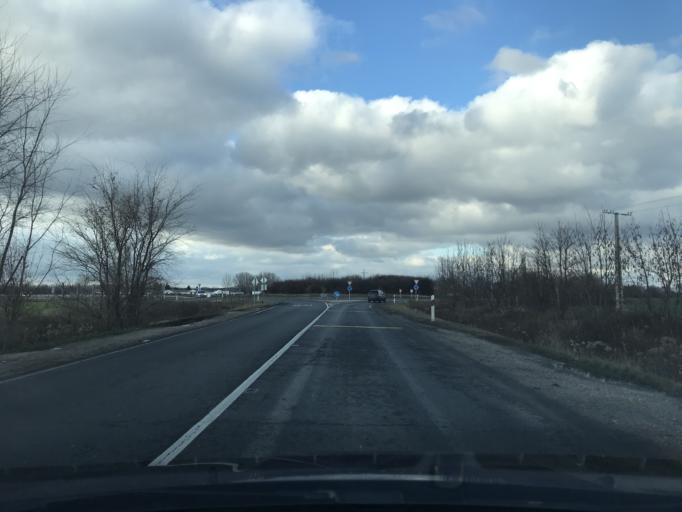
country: HU
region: Bacs-Kiskun
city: Dusnok
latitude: 46.3534
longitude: 18.9664
